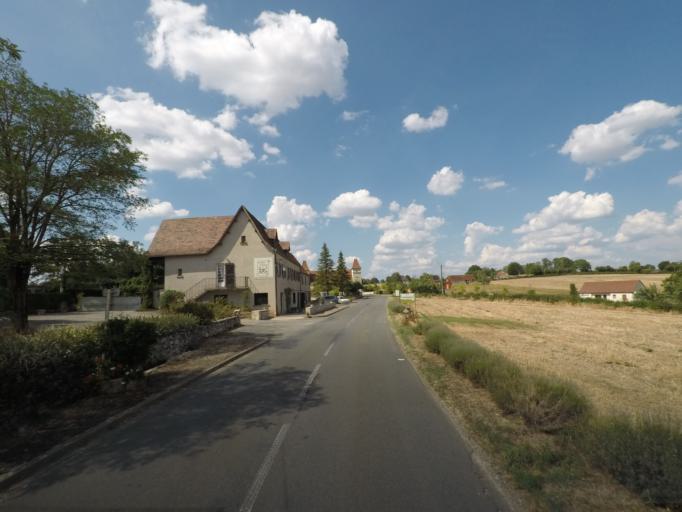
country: FR
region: Midi-Pyrenees
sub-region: Departement du Lot
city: Le Vigan
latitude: 44.6313
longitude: 1.5965
